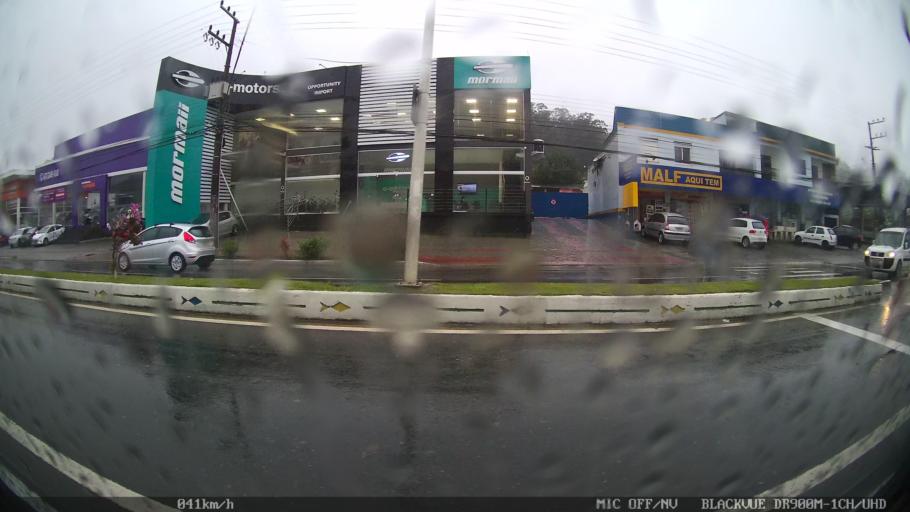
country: BR
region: Santa Catarina
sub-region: Itajai
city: Itajai
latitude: -26.9271
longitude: -48.6463
